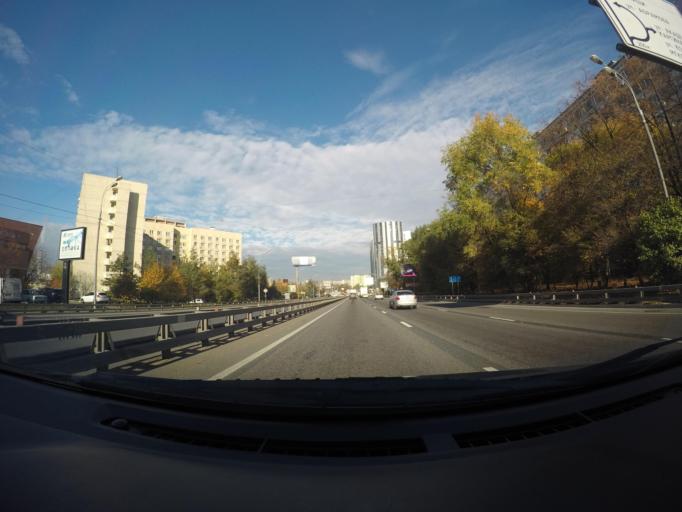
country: RU
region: Moskovskaya
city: Druzhba
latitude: 55.9135
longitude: 37.7741
